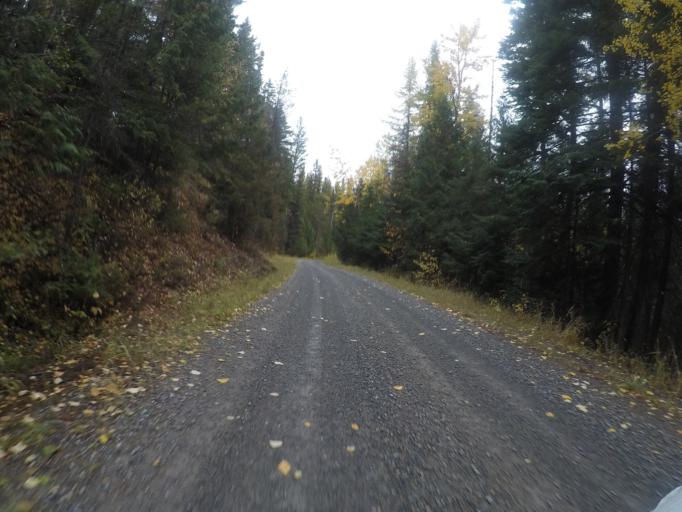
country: US
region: Montana
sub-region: Flathead County
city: Bigfork
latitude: 47.8811
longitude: -113.8731
